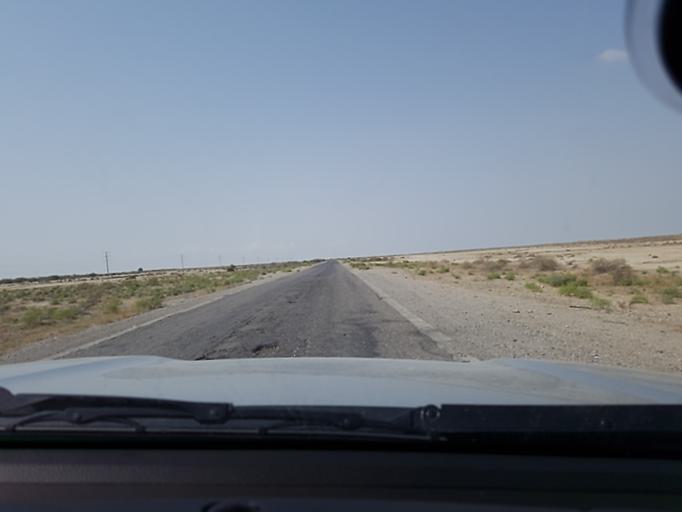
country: TM
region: Balkan
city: Gumdag
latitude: 38.7834
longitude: 54.5942
